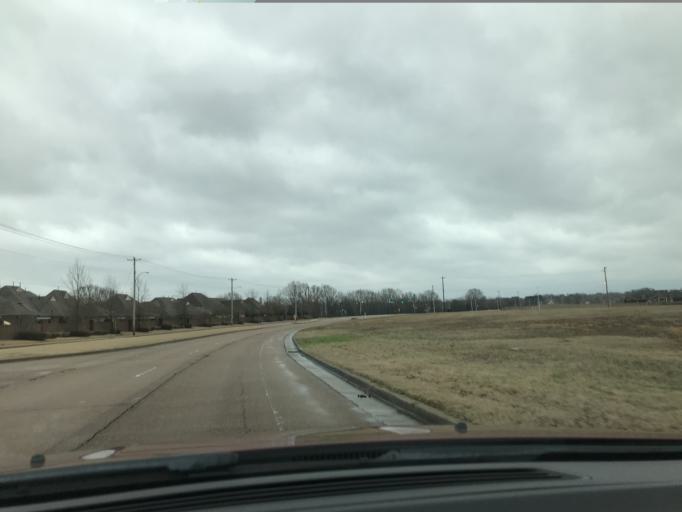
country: US
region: Tennessee
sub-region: Shelby County
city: Collierville
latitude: 35.0841
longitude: -89.6830
